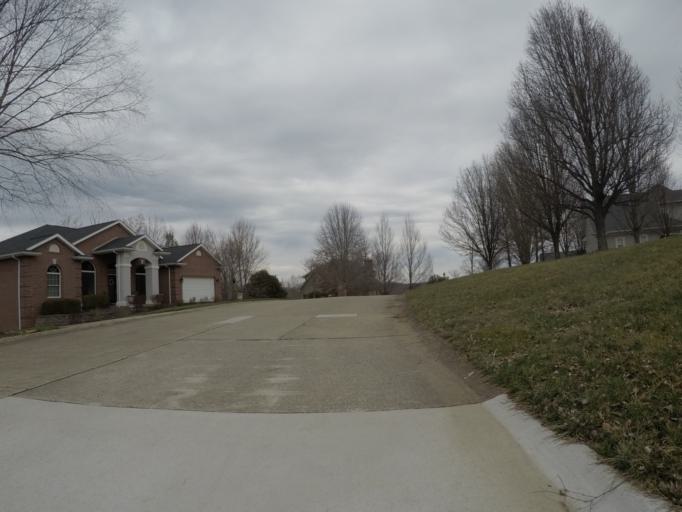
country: US
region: West Virginia
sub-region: Cabell County
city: Pea Ridge
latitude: 38.3964
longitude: -82.3789
